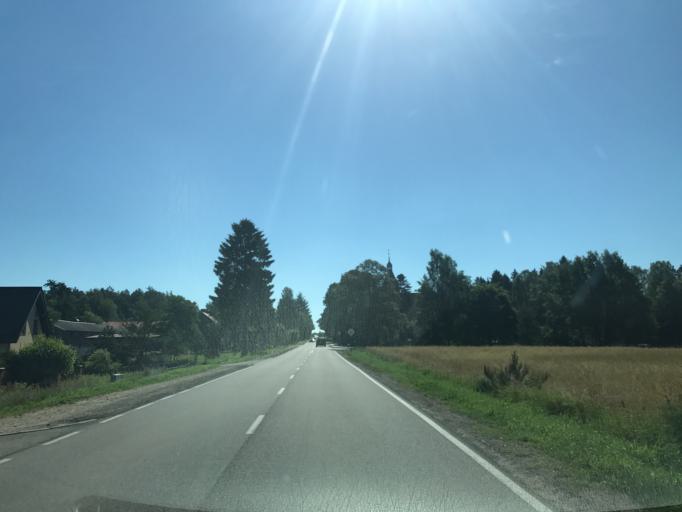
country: PL
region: Pomeranian Voivodeship
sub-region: Powiat leborski
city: Cewice
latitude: 54.3406
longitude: 17.6862
